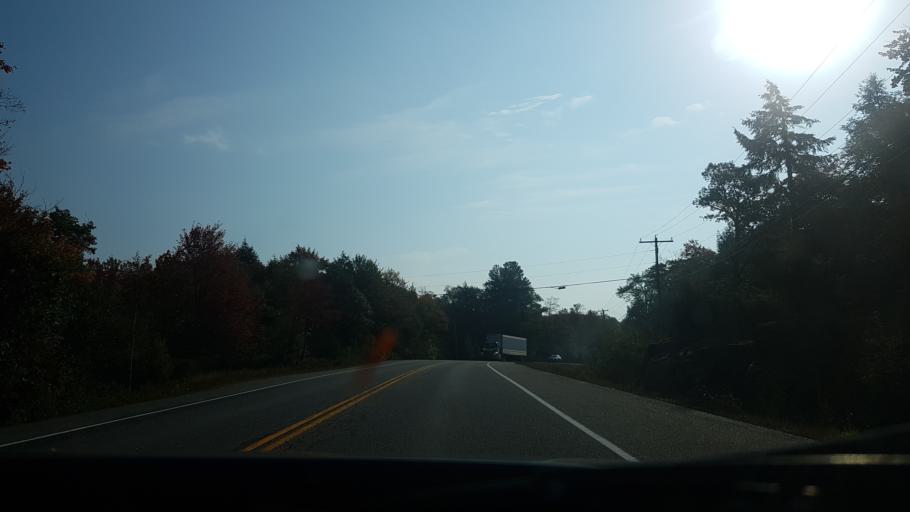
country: CA
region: Ontario
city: Bracebridge
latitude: 45.2434
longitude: -79.5941
